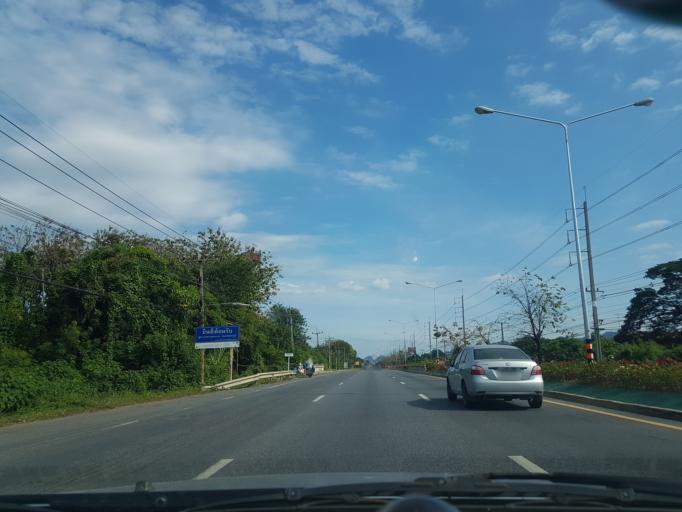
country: TH
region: Sara Buri
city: Phra Phutthabat
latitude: 14.7421
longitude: 100.7624
